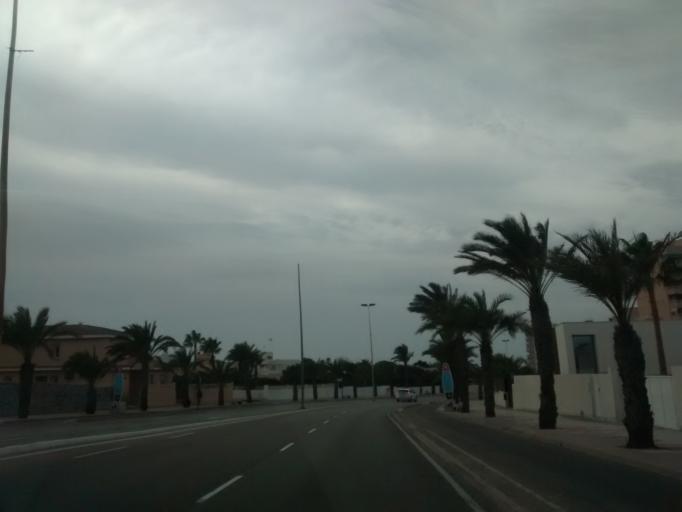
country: ES
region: Murcia
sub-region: Murcia
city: La Manga del Mar Menor
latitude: 37.6673
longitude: -0.7279
